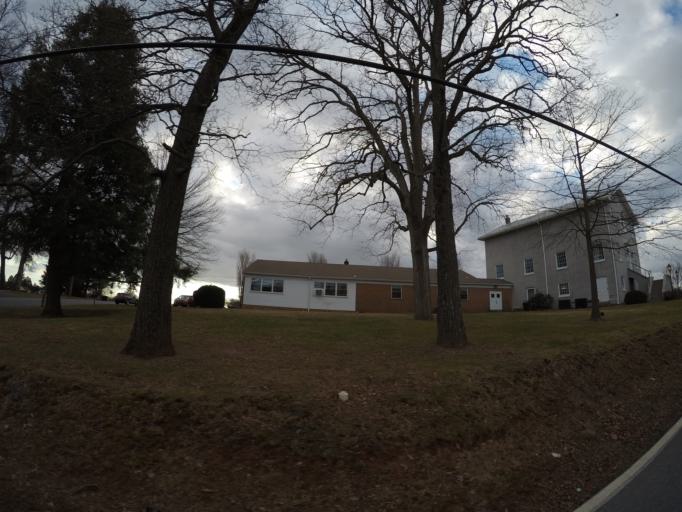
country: US
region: Maryland
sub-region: Carroll County
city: Sykesville
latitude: 39.3741
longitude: -76.9729
